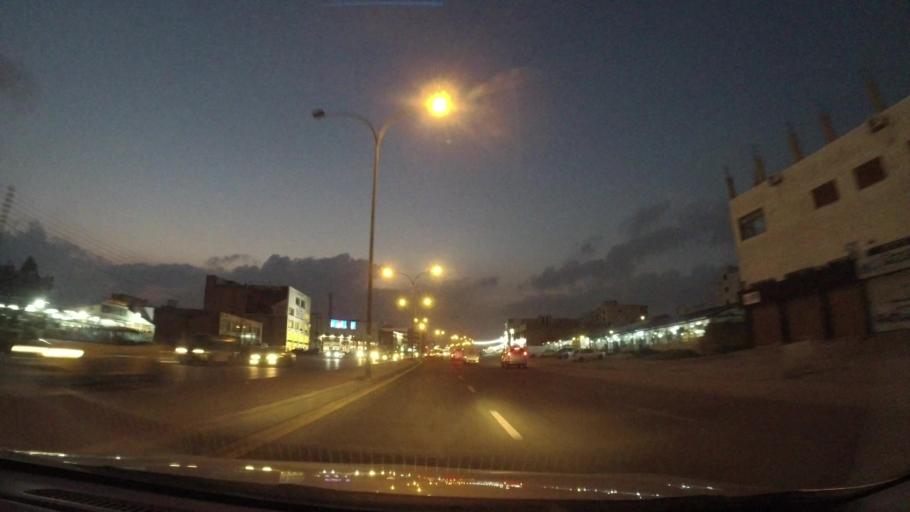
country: JO
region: Amman
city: Al Bunayyat ash Shamaliyah
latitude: 31.8991
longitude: 35.8970
